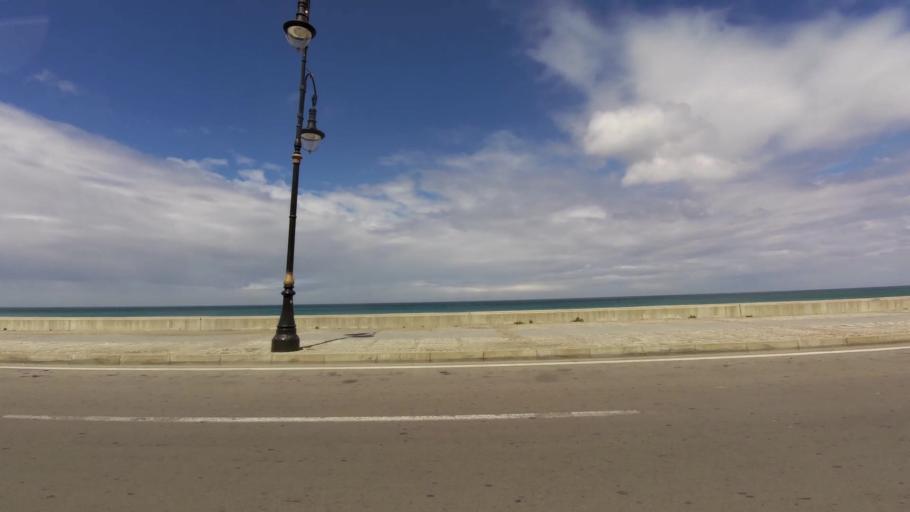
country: MA
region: Tanger-Tetouan
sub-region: Tanger-Assilah
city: Tangier
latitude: 35.7922
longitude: -5.8209
